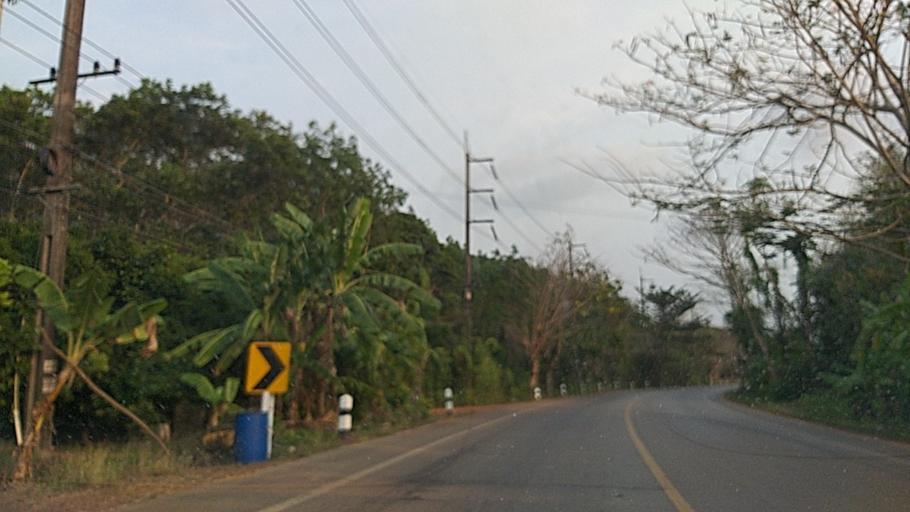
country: TH
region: Trat
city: Laem Ngop
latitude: 12.2503
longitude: 102.2927
